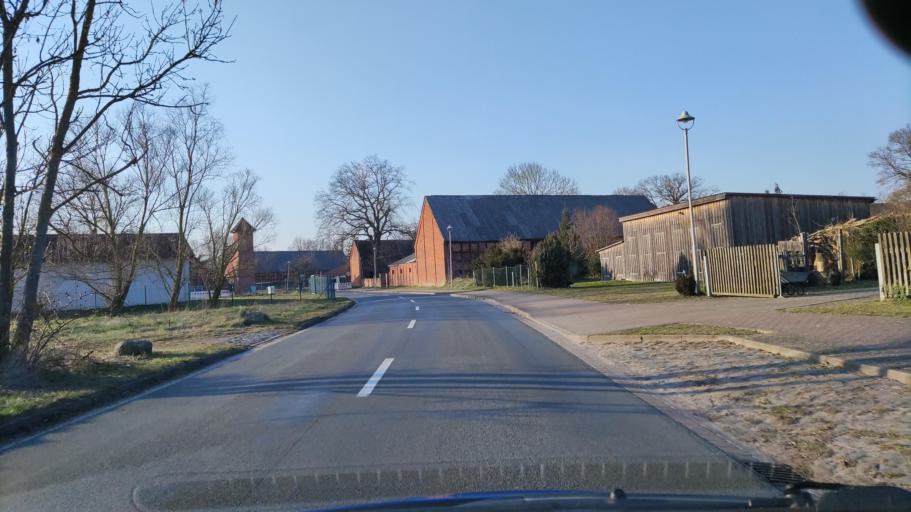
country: DE
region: Brandenburg
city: Cumlosen
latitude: 52.9908
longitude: 11.6067
